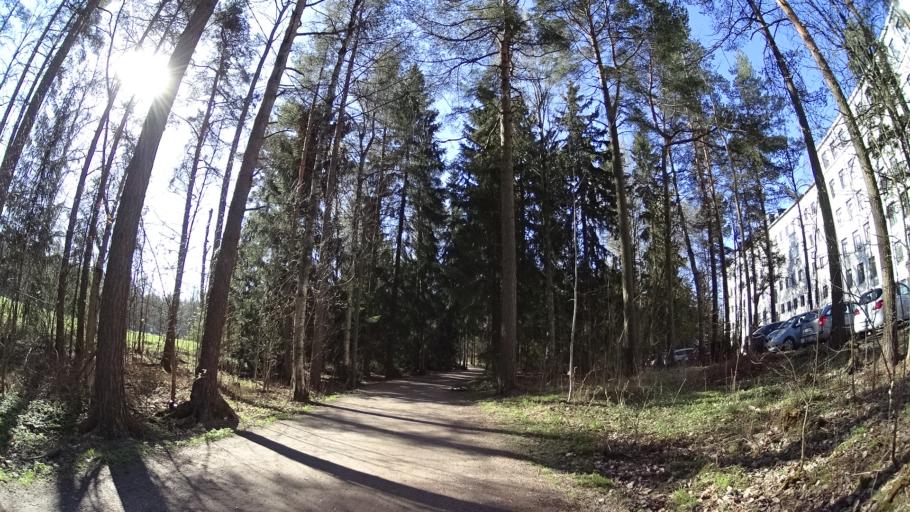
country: FI
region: Uusimaa
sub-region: Helsinki
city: Helsinki
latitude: 60.2024
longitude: 24.9094
